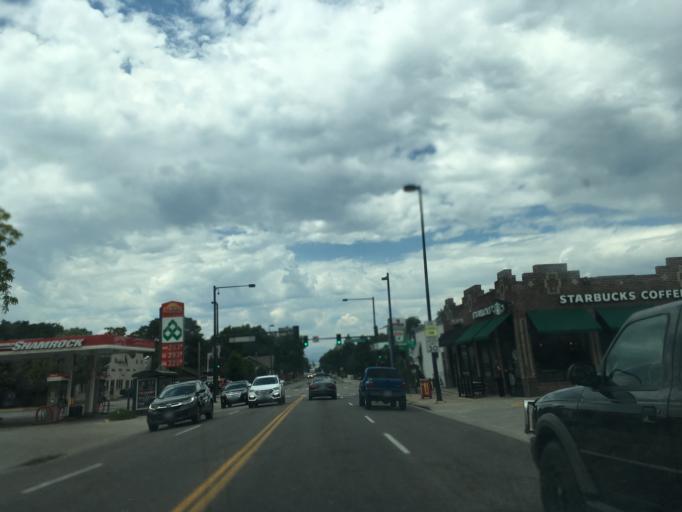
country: US
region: Colorado
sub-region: Denver County
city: Denver
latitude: 39.7112
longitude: -104.9725
